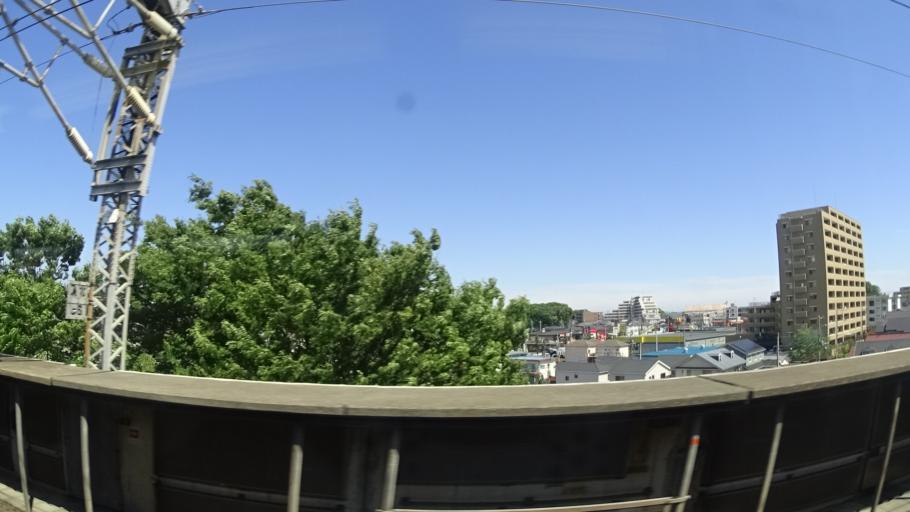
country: JP
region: Saitama
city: Ageoshimo
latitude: 35.9472
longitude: 139.6192
